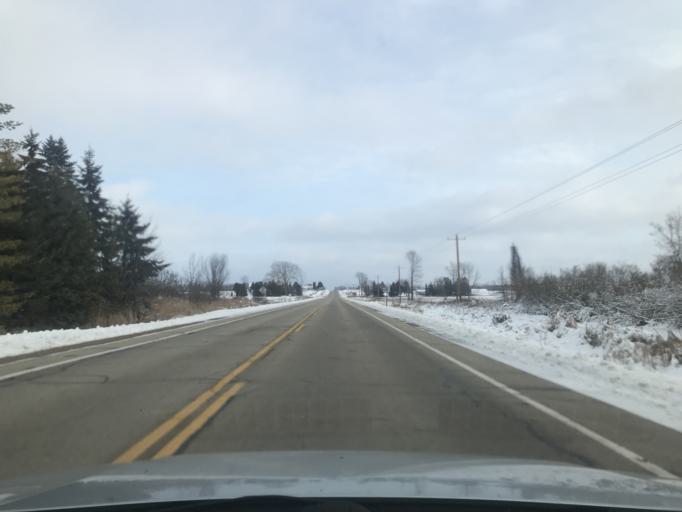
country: US
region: Wisconsin
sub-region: Oconto County
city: Oconto
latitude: 44.8935
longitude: -87.9949
